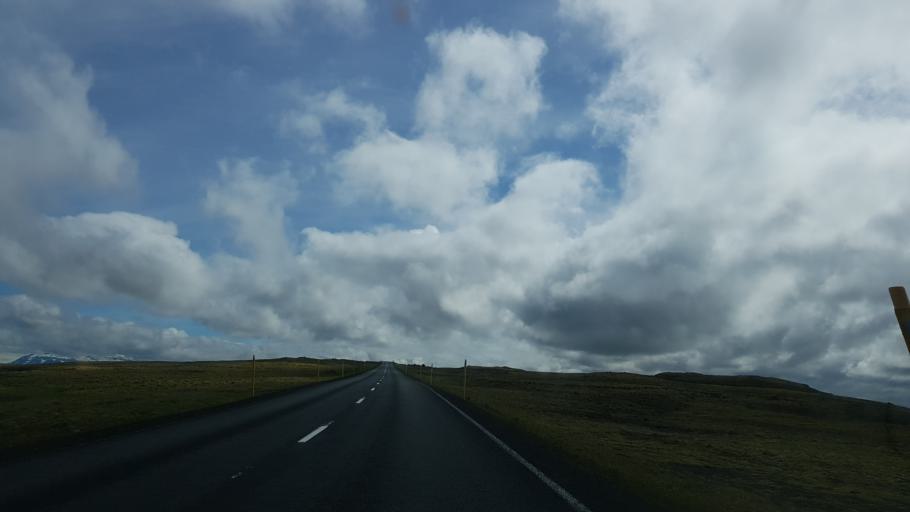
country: IS
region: West
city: Borgarnes
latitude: 64.9970
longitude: -21.0671
